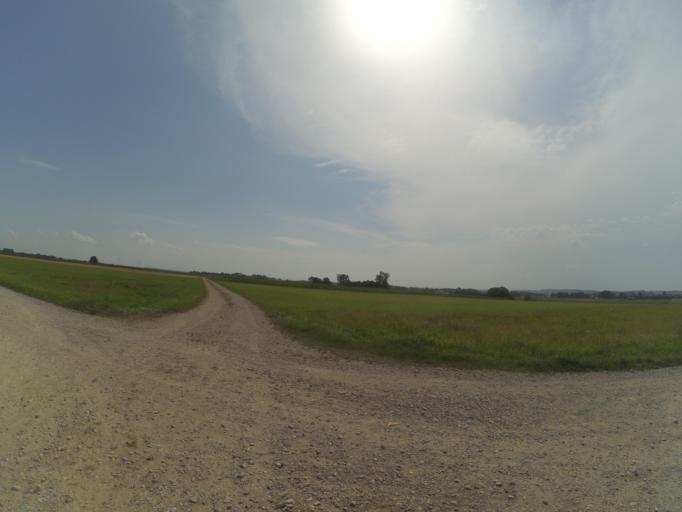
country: DE
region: Bavaria
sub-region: Swabia
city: Jengen
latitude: 48.0156
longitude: 10.7326
